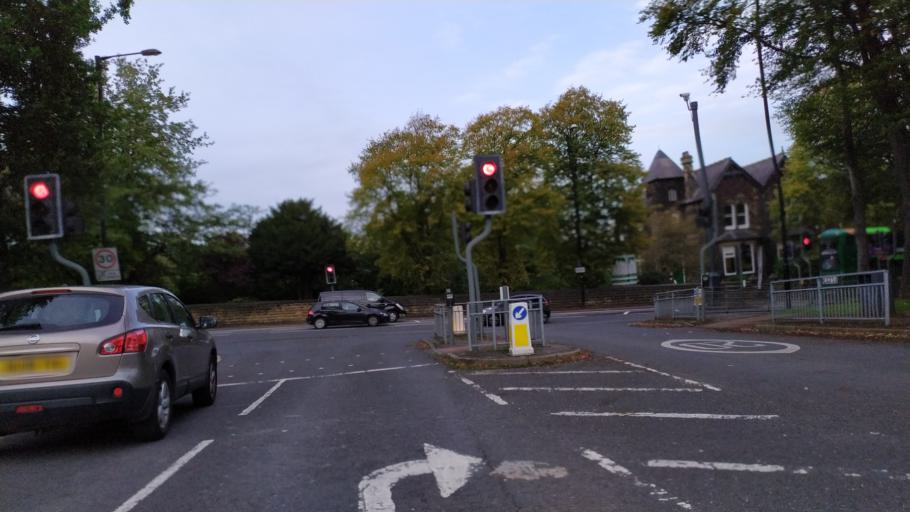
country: GB
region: England
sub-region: City and Borough of Leeds
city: Chapel Allerton
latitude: 53.8311
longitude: -1.5883
